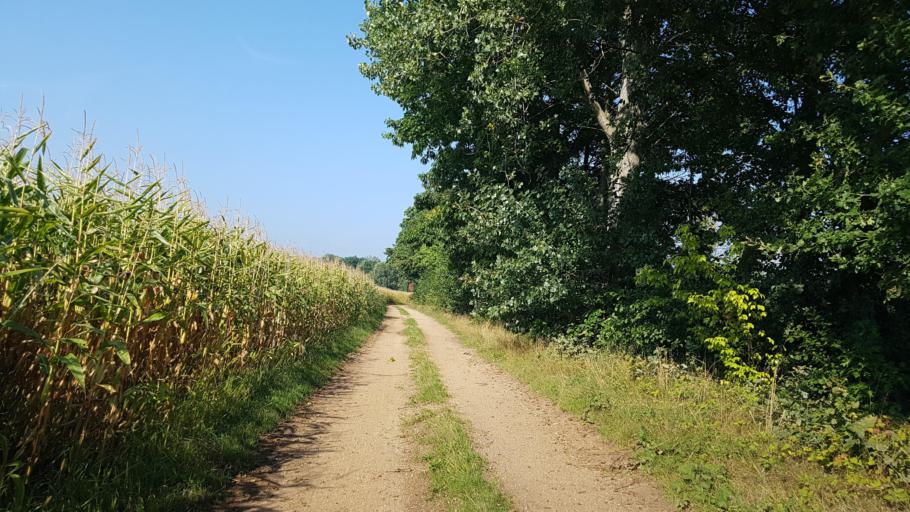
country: DE
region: Brandenburg
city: Luckau
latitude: 51.7981
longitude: 13.6566
